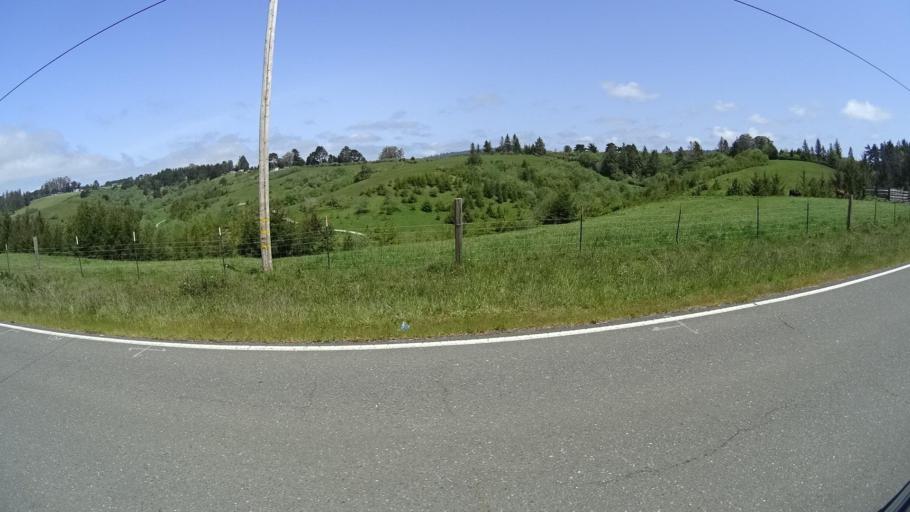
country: US
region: California
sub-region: Humboldt County
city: Fortuna
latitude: 40.6435
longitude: -124.2140
